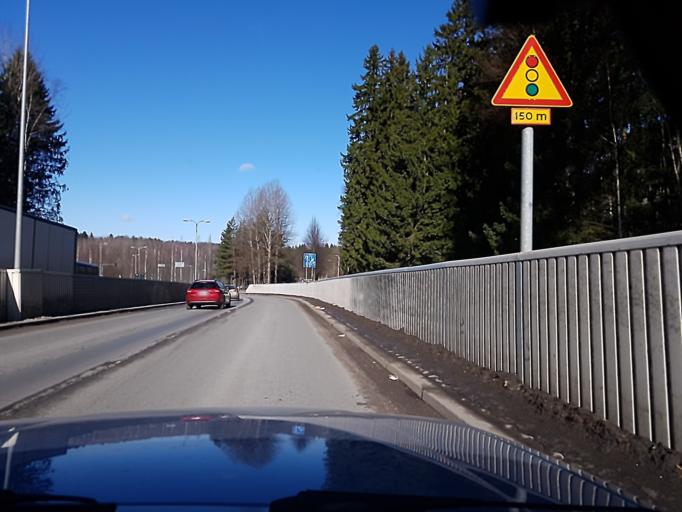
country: FI
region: Uusimaa
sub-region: Helsinki
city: Teekkarikylae
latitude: 60.2641
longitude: 24.8675
